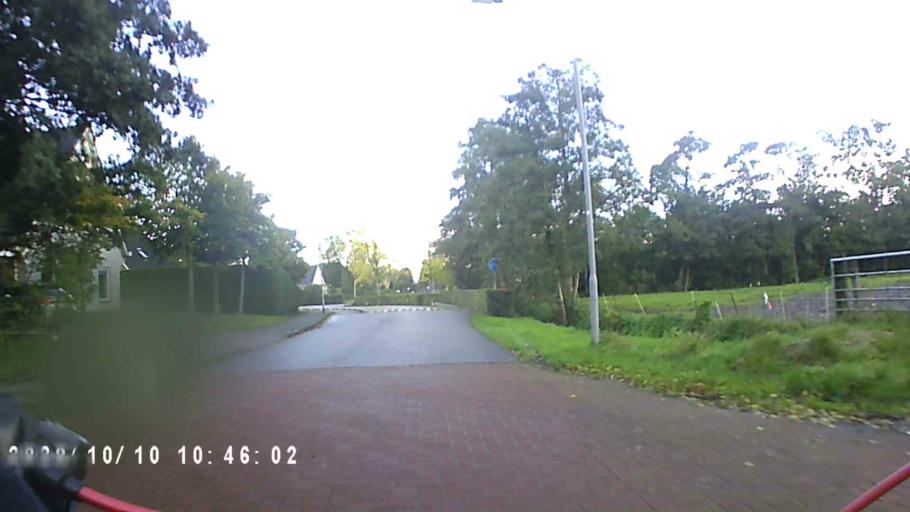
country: NL
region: Groningen
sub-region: Gemeente Grootegast
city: Grootegast
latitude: 53.1691
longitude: 6.2543
